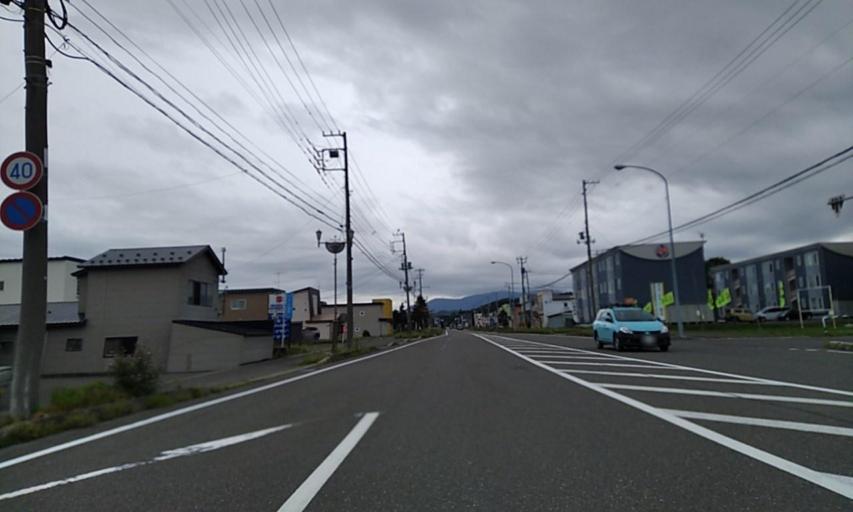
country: JP
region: Hokkaido
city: Obihiro
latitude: 42.3011
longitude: 143.3161
